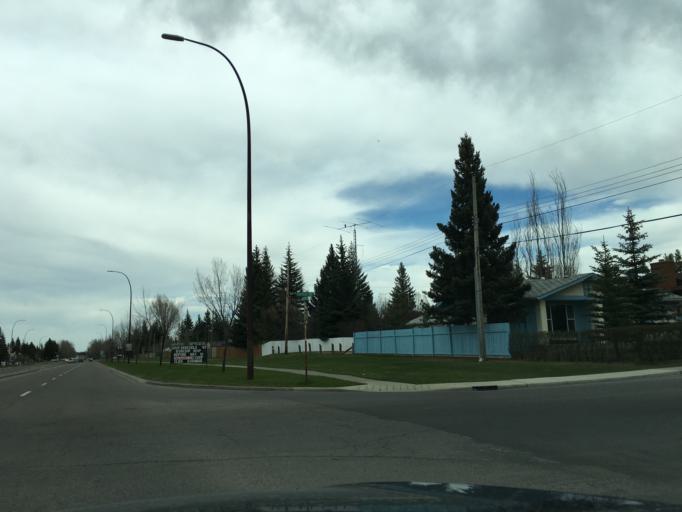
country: CA
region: Alberta
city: Calgary
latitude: 50.9612
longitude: -114.1245
